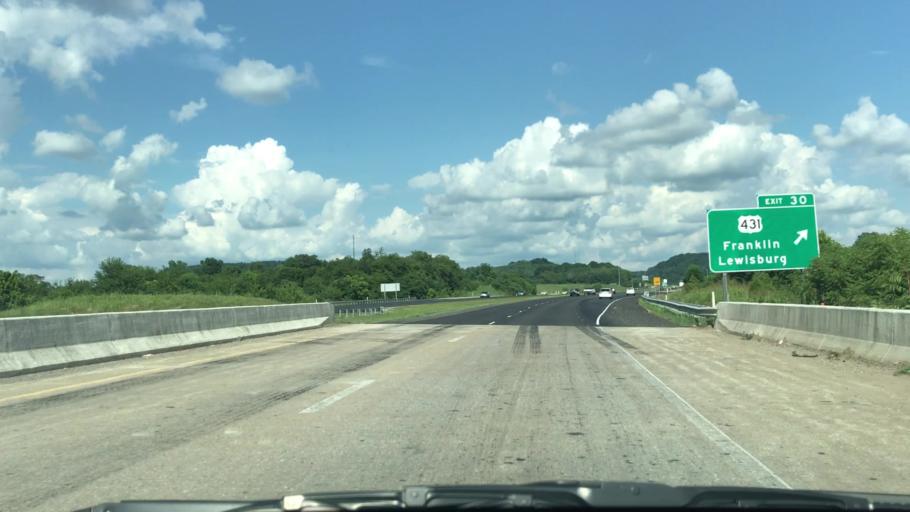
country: US
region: Tennessee
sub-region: Williamson County
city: Thompson's Station
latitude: 35.8216
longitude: -86.8614
